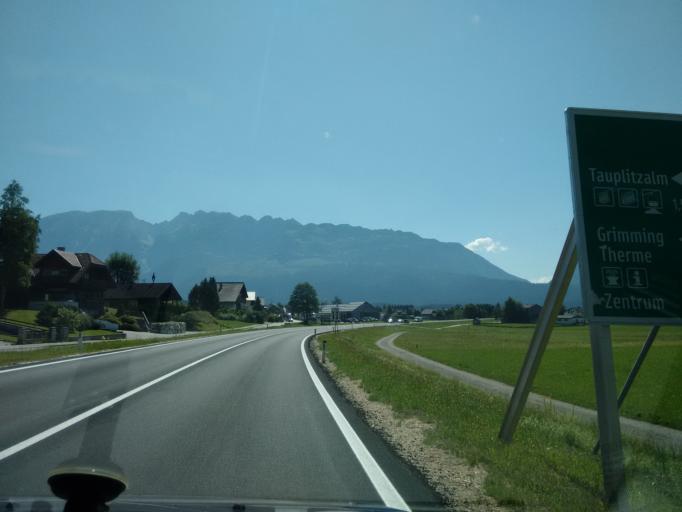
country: AT
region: Styria
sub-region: Politischer Bezirk Liezen
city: Tauplitz
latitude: 47.5595
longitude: 13.9224
